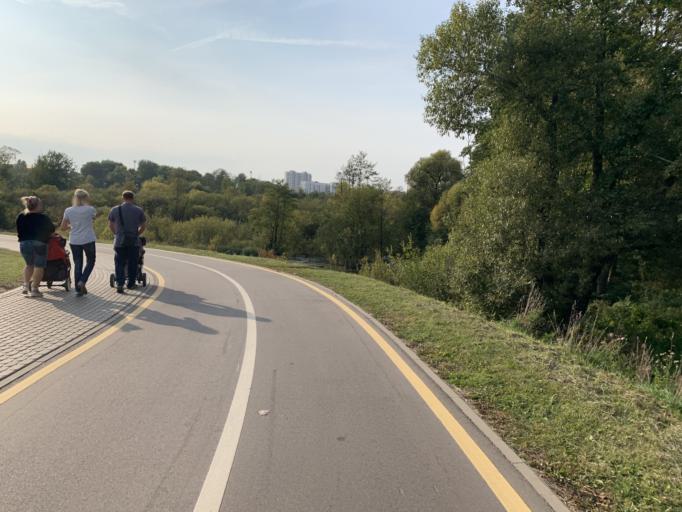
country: BY
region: Minsk
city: Minsk
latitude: 53.8612
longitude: 27.5867
